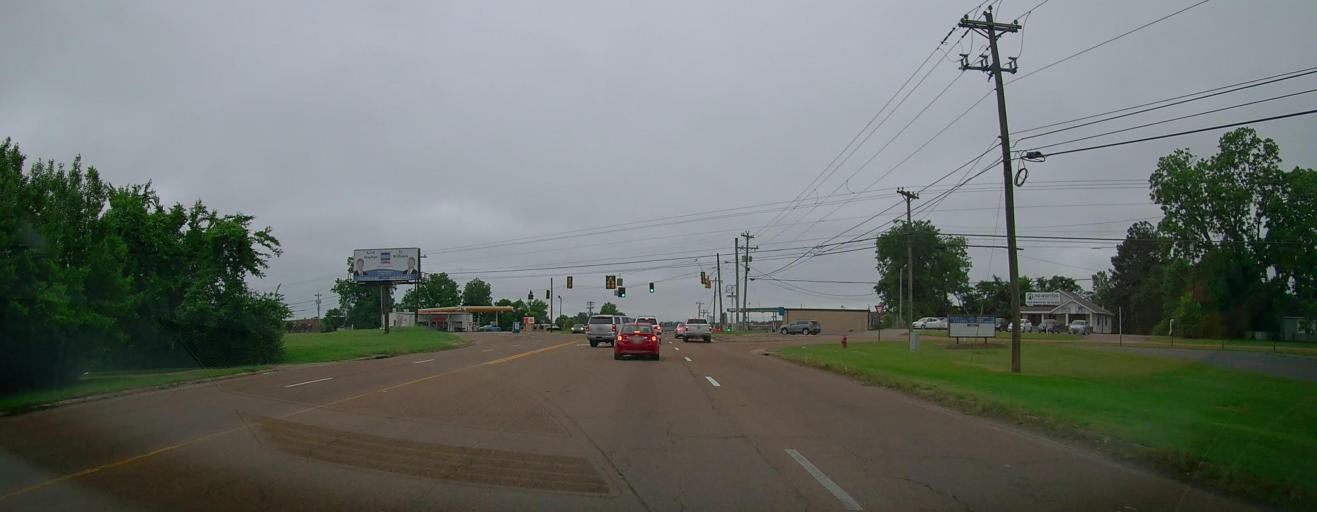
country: US
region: Mississippi
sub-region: De Soto County
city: Olive Branch
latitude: 34.9335
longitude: -89.7949
